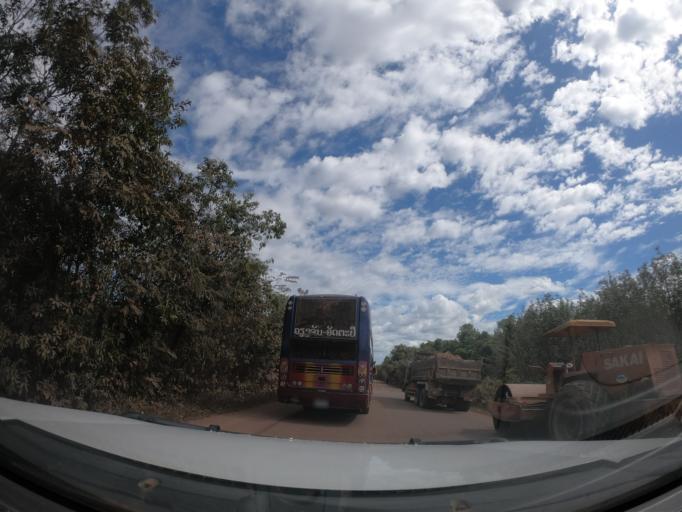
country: LA
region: Bolikhamxai
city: Muang Pakxan
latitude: 18.4408
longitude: 103.5245
